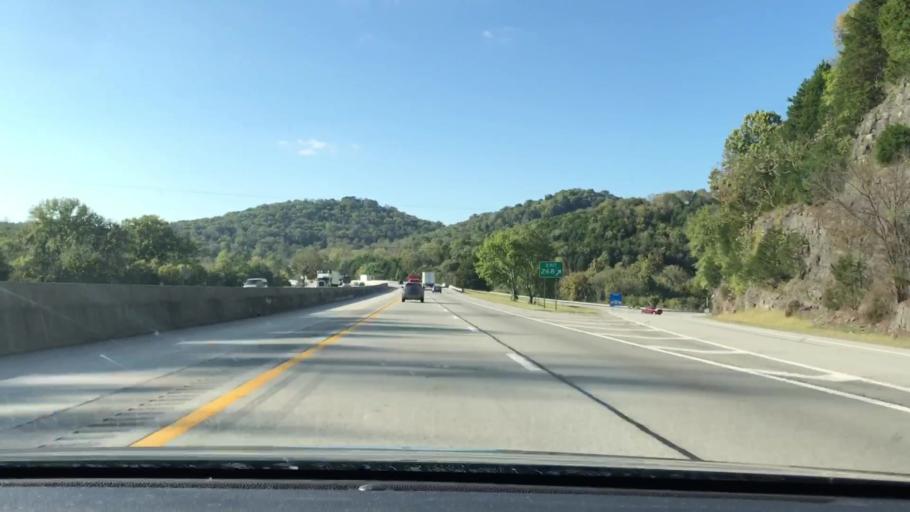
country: US
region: Tennessee
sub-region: Putnam County
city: Lafayette
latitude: 36.1368
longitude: -85.7864
